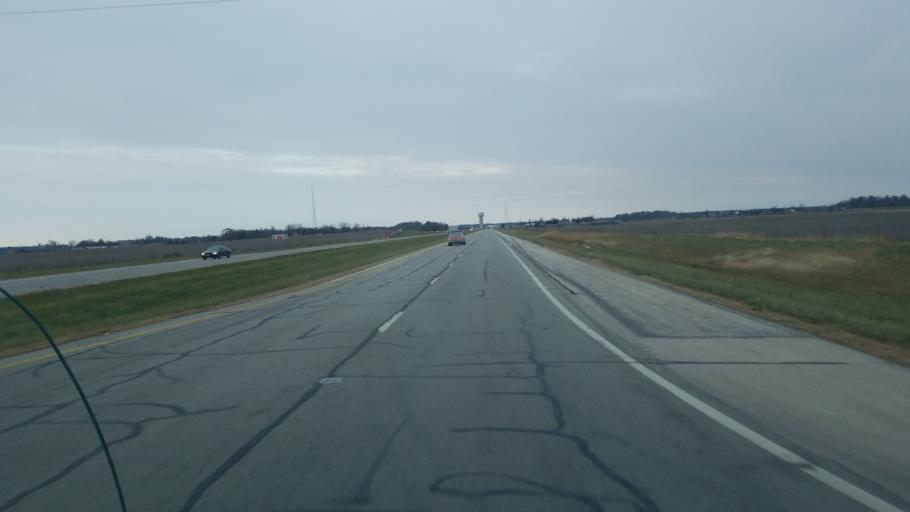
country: US
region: Ohio
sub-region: Mercer County
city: Celina
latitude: 40.5574
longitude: -84.4940
